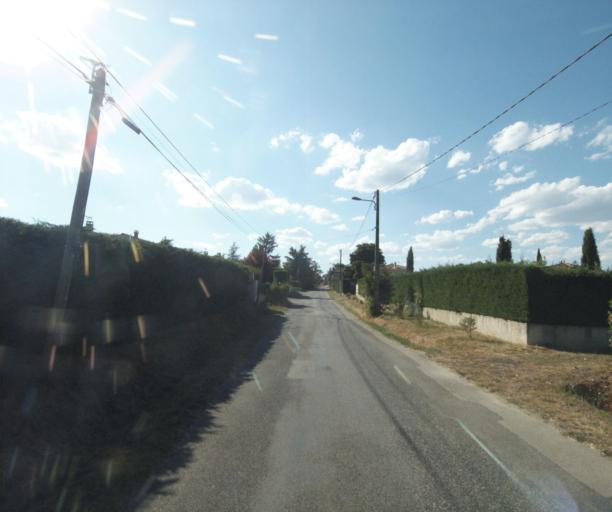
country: FR
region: Rhone-Alpes
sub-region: Departement du Rhone
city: Lentilly
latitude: 45.8071
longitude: 4.6837
